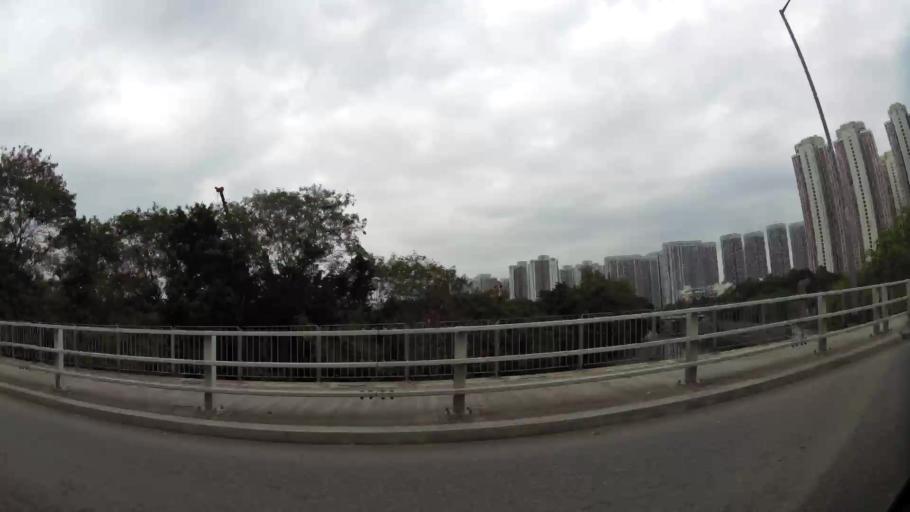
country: HK
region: Yuen Long
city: Yuen Long Kau Hui
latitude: 22.4467
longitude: 113.9974
